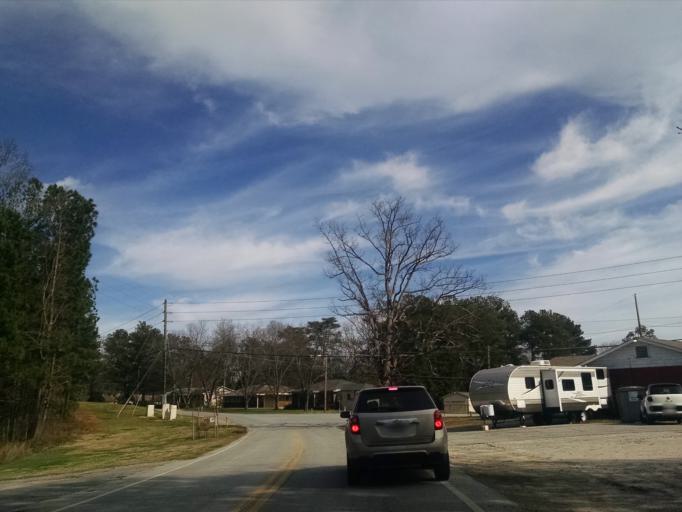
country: US
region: Georgia
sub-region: Gwinnett County
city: Sugar Hill
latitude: 34.0948
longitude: -84.0314
